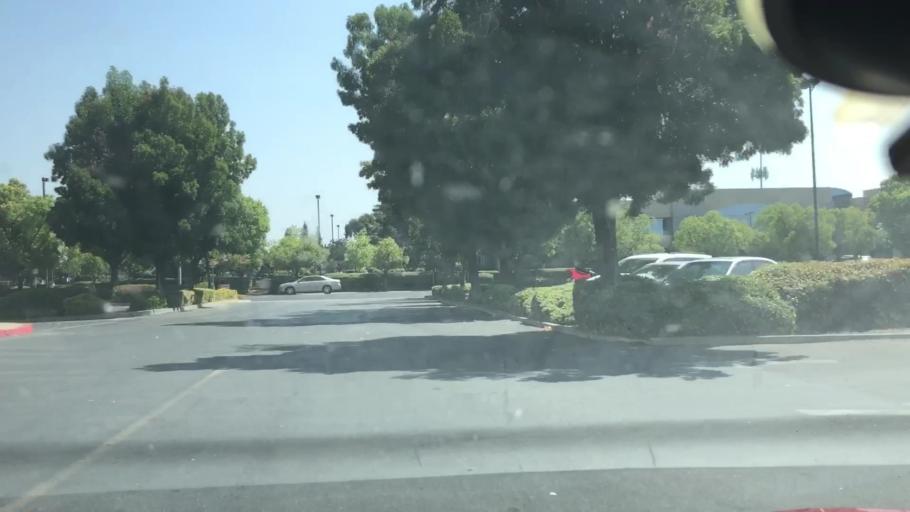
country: US
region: California
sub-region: San Joaquin County
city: Lincoln Village
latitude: 37.9990
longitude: -121.3111
